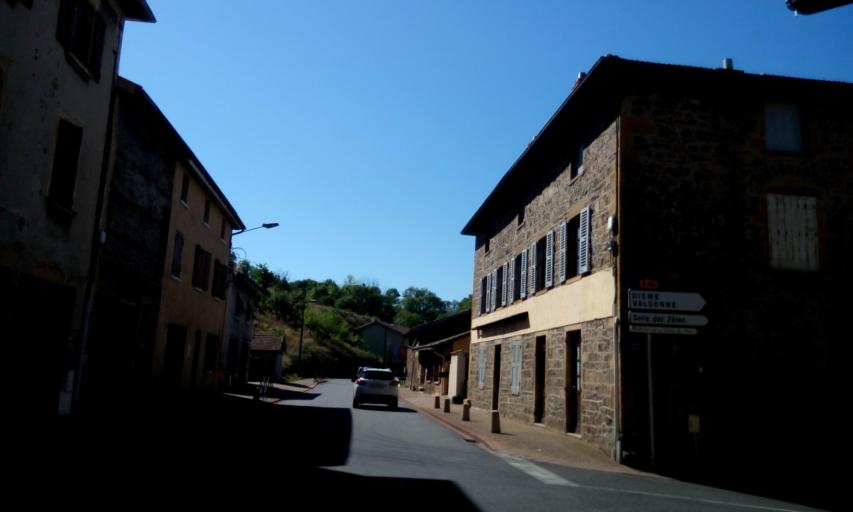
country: FR
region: Rhone-Alpes
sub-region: Departement du Rhone
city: Saint-Verand
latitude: 45.9824
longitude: 4.5088
